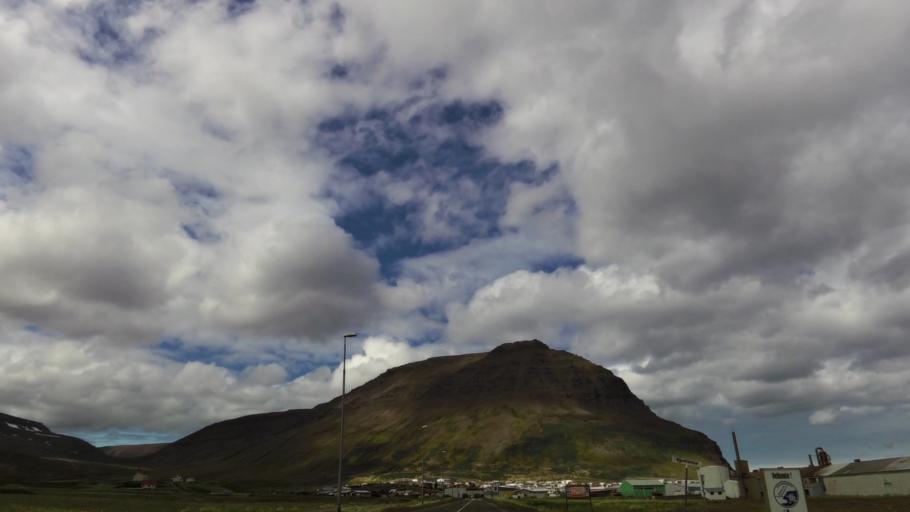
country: IS
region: Westfjords
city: Isafjoerdur
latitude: 66.1510
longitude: -23.2462
